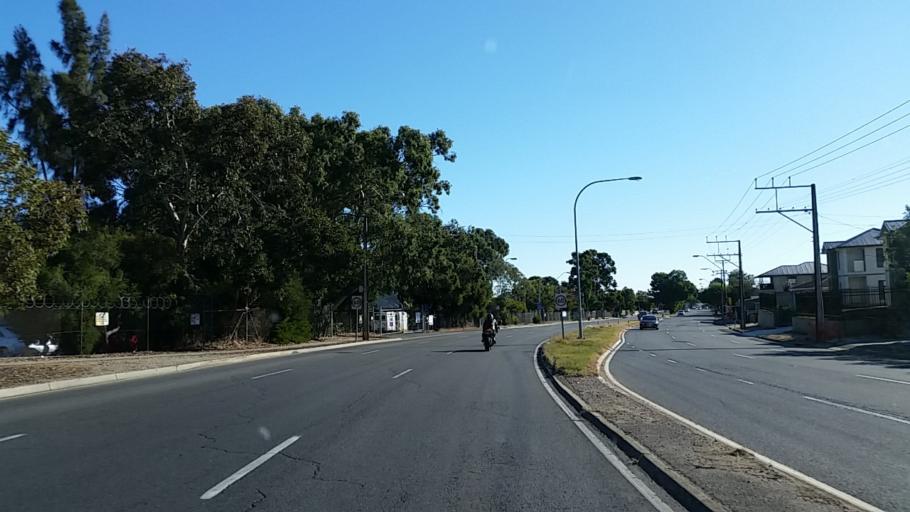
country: AU
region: South Australia
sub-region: Tea Tree Gully
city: Hope Valley
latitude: -34.8270
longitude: 138.7063
